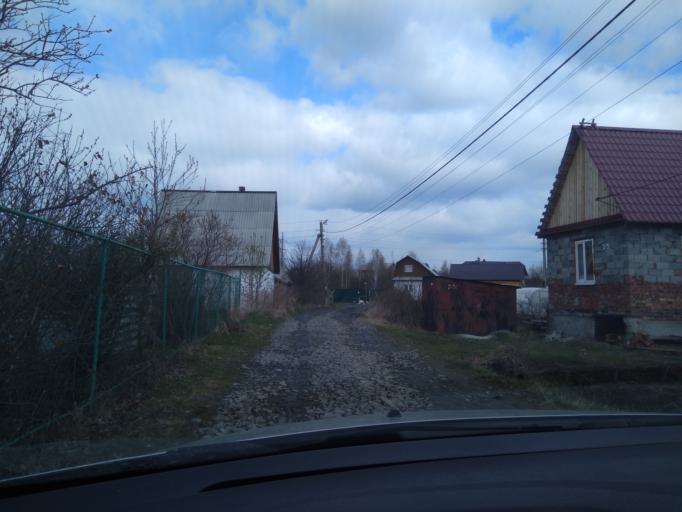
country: RU
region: Sverdlovsk
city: Sredneuralsk
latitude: 56.9719
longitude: 60.4665
